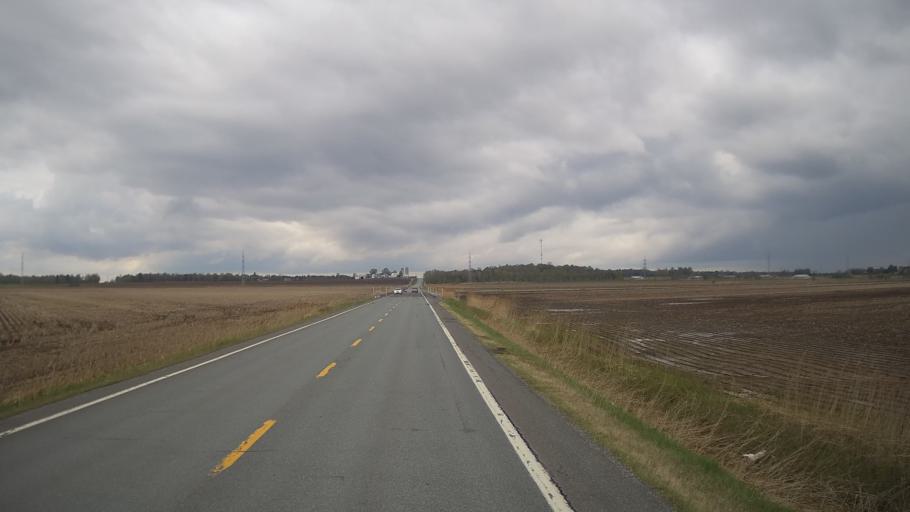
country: CA
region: Quebec
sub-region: Monteregie
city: Farnham
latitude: 45.2598
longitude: -72.9237
